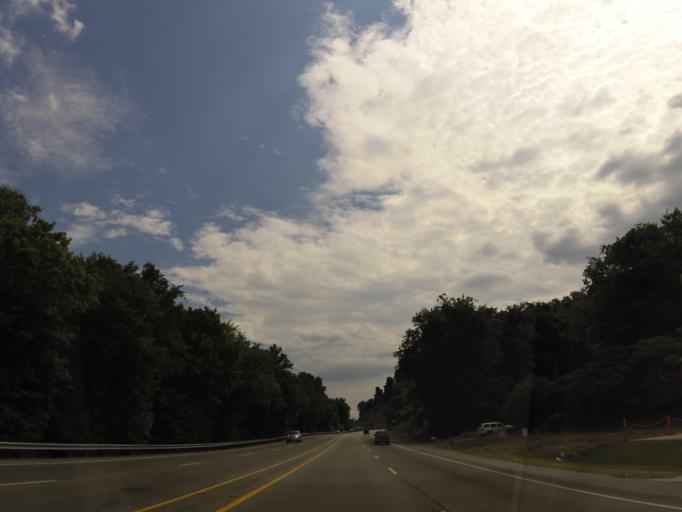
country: US
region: Tennessee
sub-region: Marion County
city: South Pittsburg
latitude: 35.0304
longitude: -85.6929
